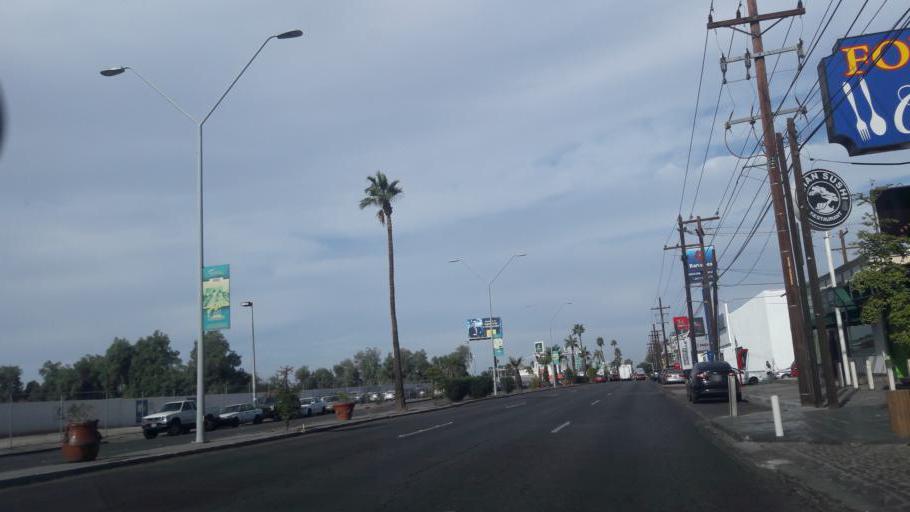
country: MX
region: Baja California
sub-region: Mexicali
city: Mexicali
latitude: 32.6509
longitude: -115.4524
